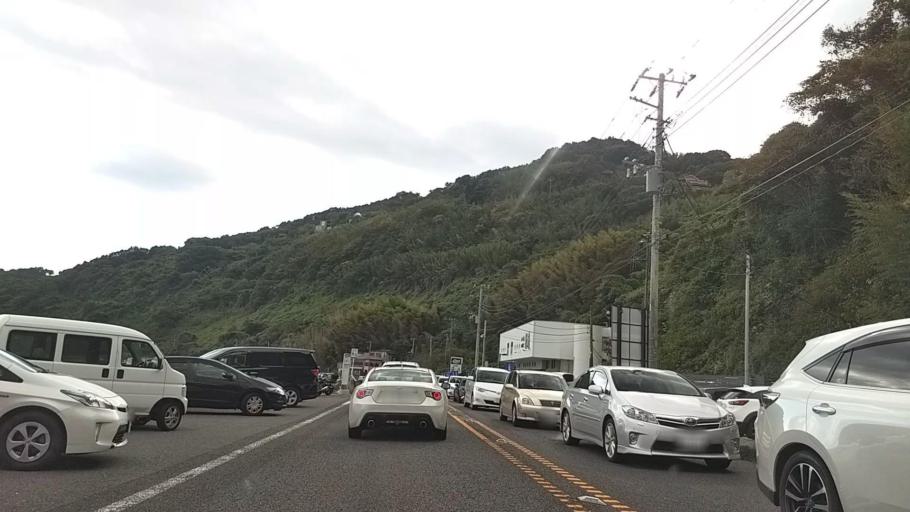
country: JP
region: Kanagawa
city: Odawara
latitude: 35.1847
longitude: 139.1364
